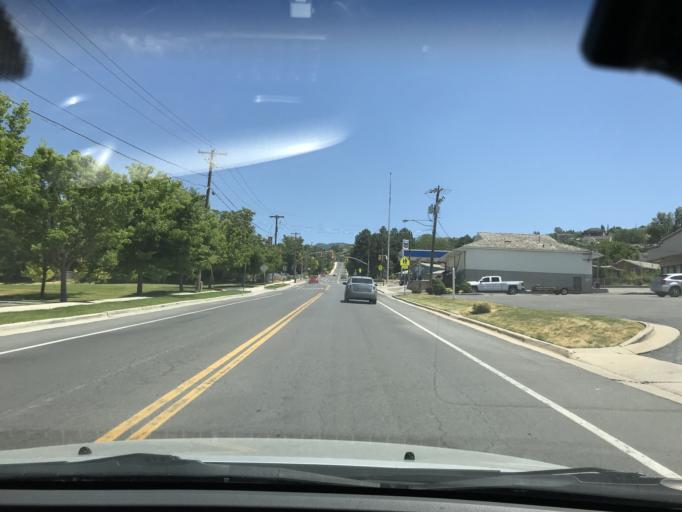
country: US
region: Utah
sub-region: Davis County
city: North Salt Lake
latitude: 40.8418
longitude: -111.9071
